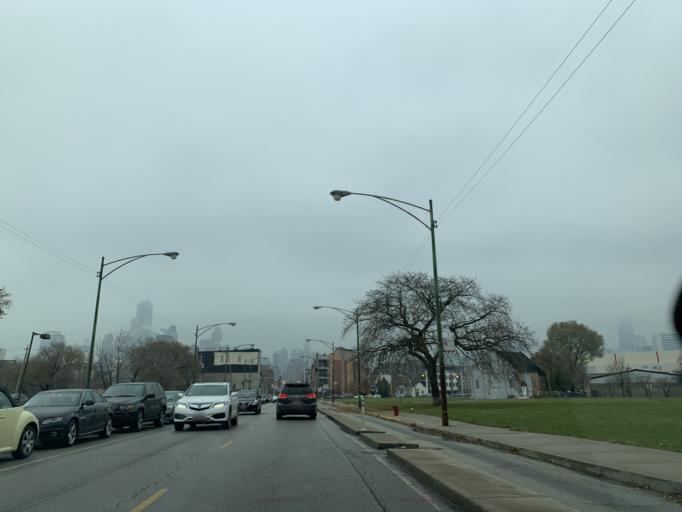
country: US
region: Illinois
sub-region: Cook County
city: Chicago
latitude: 41.9075
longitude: -87.6445
